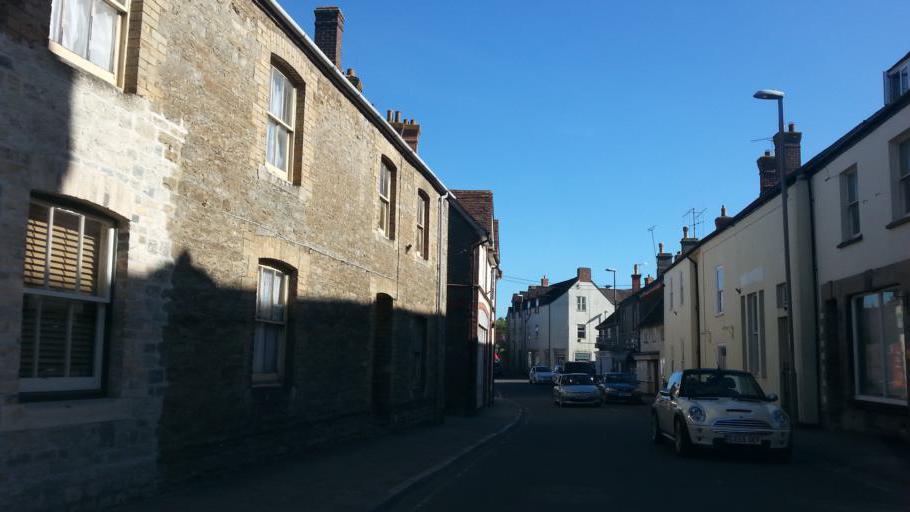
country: GB
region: England
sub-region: Dorset
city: Stalbridge
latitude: 50.9600
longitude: -2.3785
